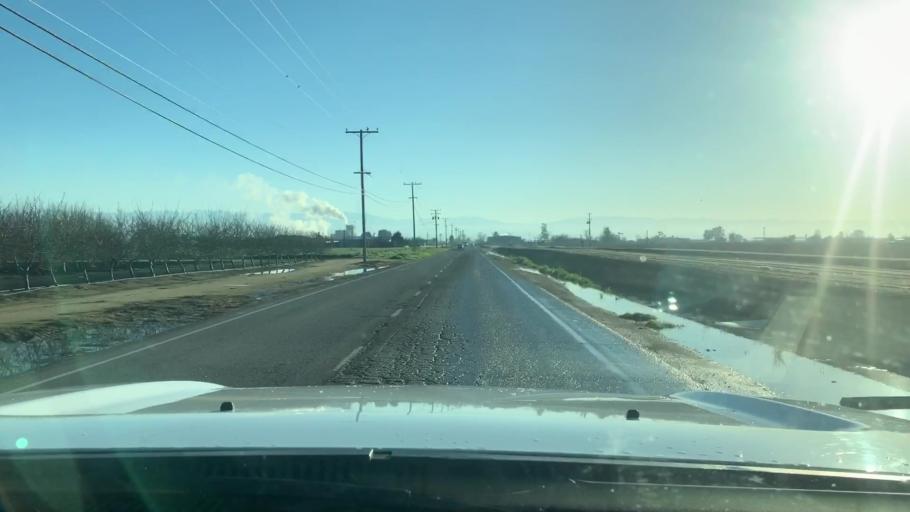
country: US
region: California
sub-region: Tulare County
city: Tulare
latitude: 36.1820
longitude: -119.3518
